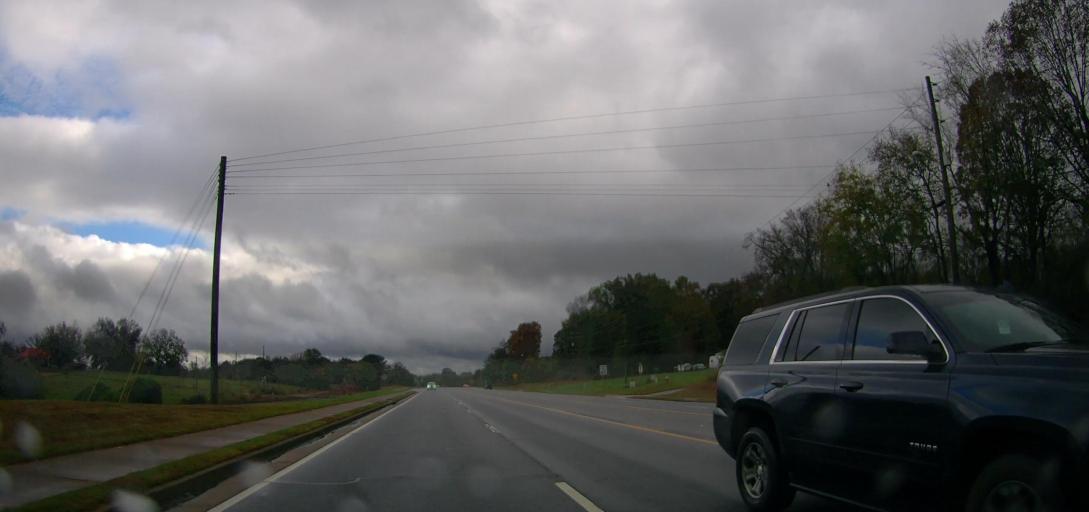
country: US
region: Georgia
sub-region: Jackson County
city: Nicholson
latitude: 34.1058
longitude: -83.4334
